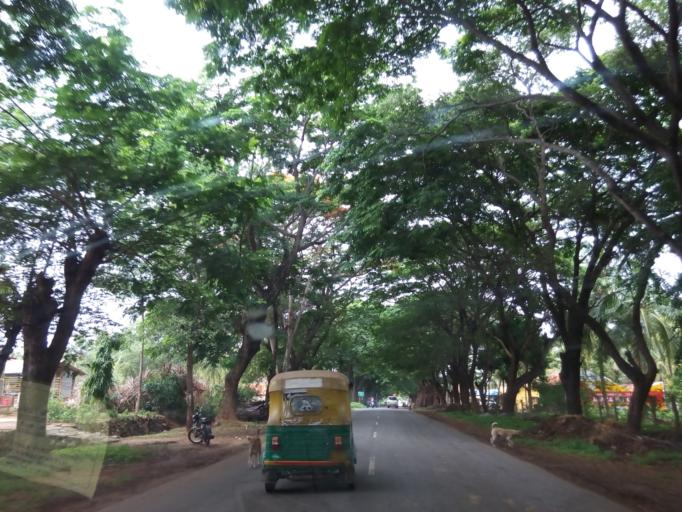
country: IN
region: Karnataka
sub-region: Hassan
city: Channarayapatna
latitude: 12.8770
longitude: 76.4274
